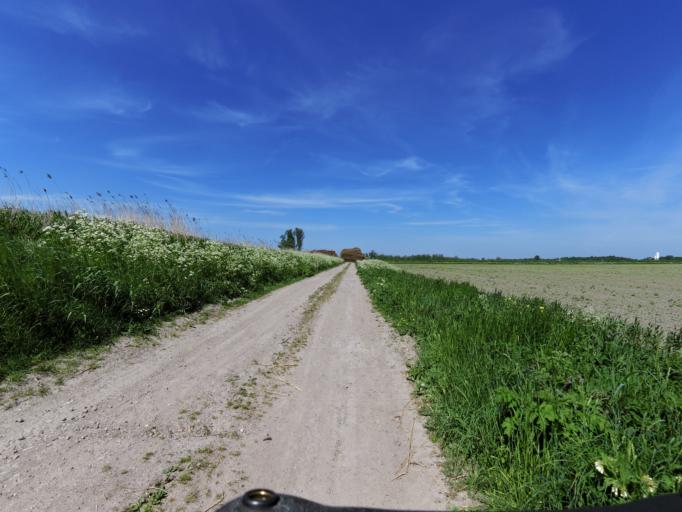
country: NL
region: South Holland
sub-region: Gemeente Binnenmaas
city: Heinenoord
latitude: 51.8281
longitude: 4.4961
